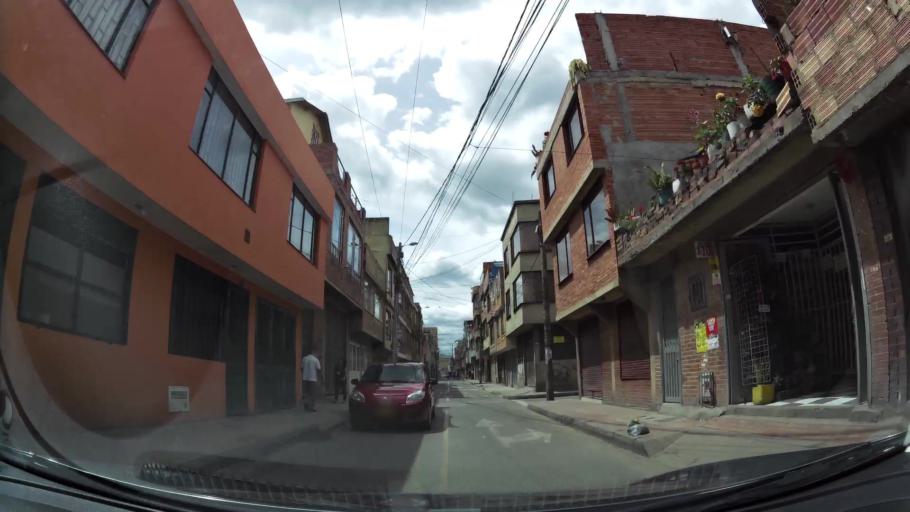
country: CO
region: Cundinamarca
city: Funza
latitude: 4.7150
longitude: -74.1376
